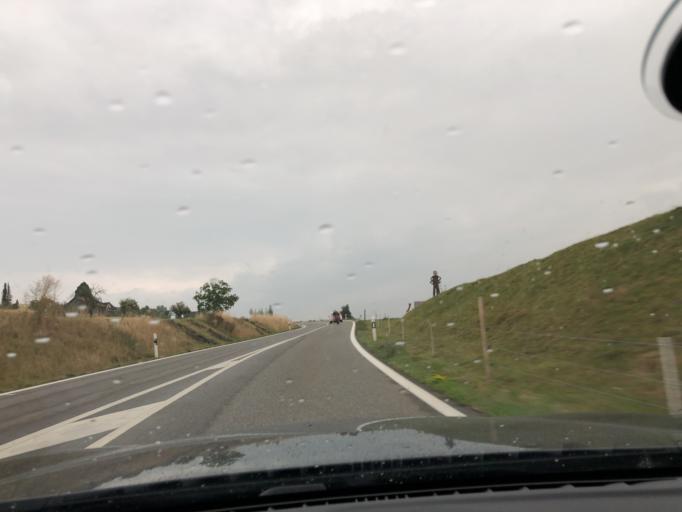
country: CH
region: Aargau
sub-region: Bezirk Bremgarten
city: Berikon
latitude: 47.3461
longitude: 8.3748
